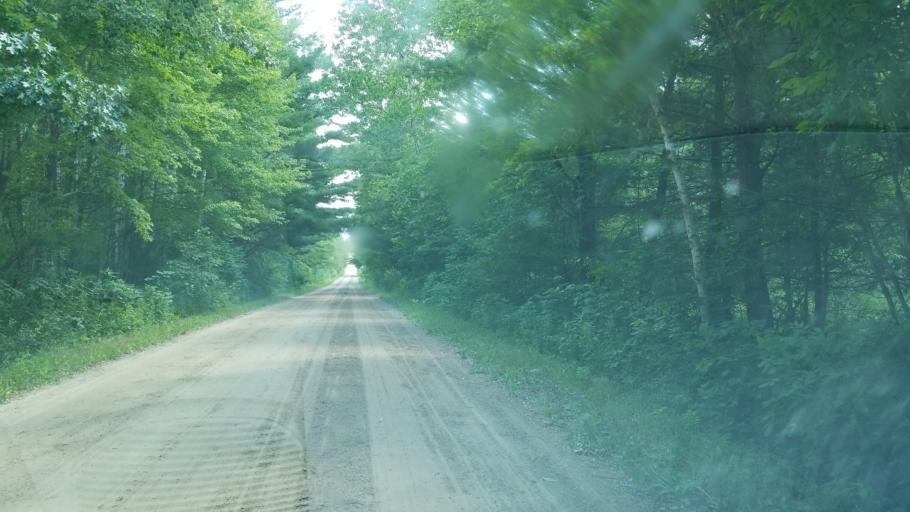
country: US
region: Michigan
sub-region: Mecosta County
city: Canadian Lakes
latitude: 43.5692
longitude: -85.3927
